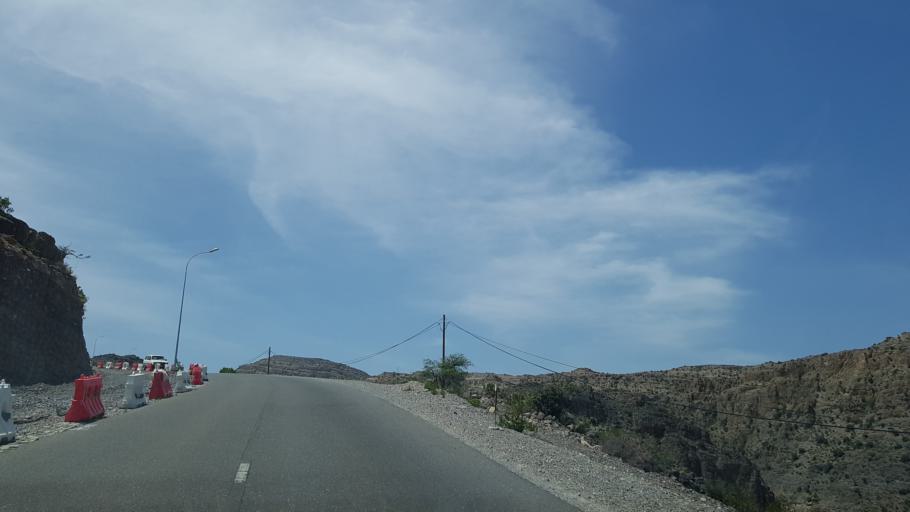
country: OM
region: Muhafazat ad Dakhiliyah
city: Izki
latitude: 23.0950
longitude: 57.6788
